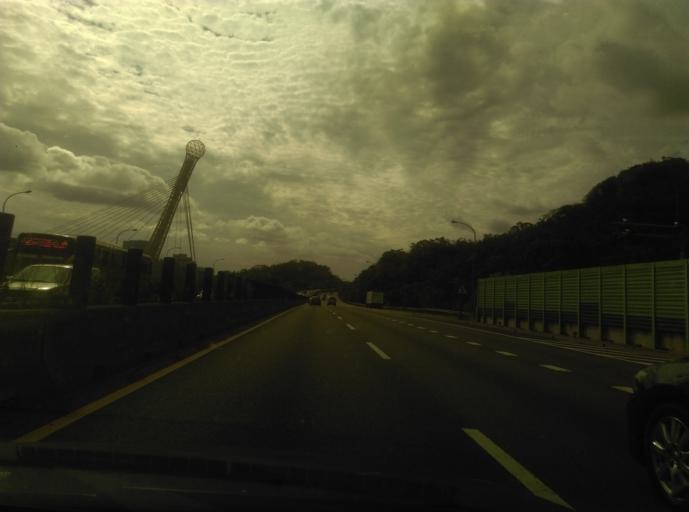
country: TW
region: Taiwan
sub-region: Keelung
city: Keelung
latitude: 25.0790
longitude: 121.6640
